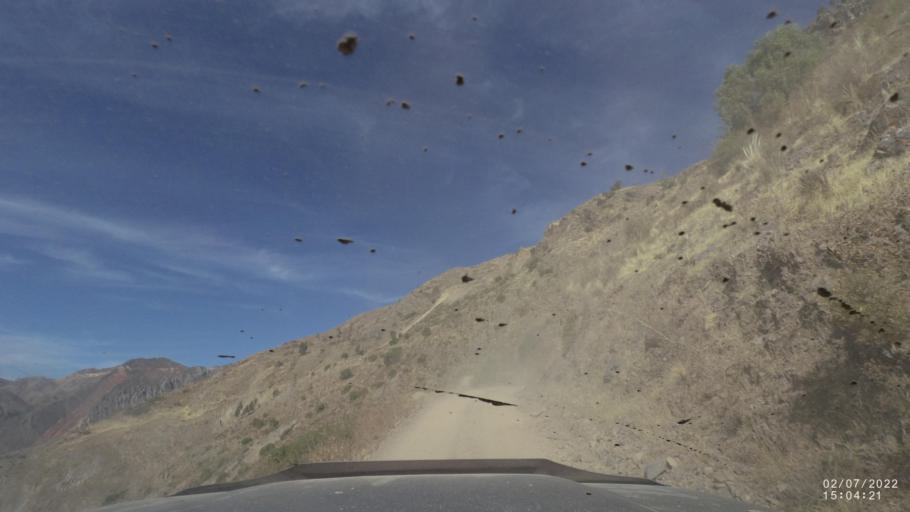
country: BO
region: Cochabamba
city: Irpa Irpa
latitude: -17.8604
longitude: -66.4358
